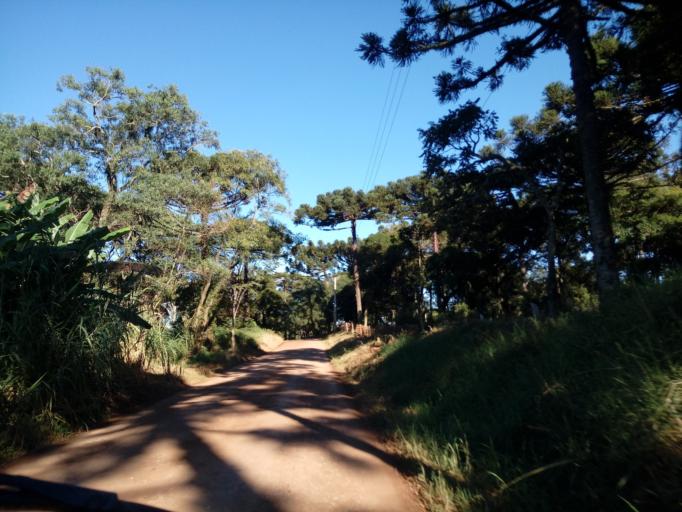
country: BR
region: Santa Catarina
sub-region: Chapeco
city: Chapeco
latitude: -27.1926
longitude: -52.6625
